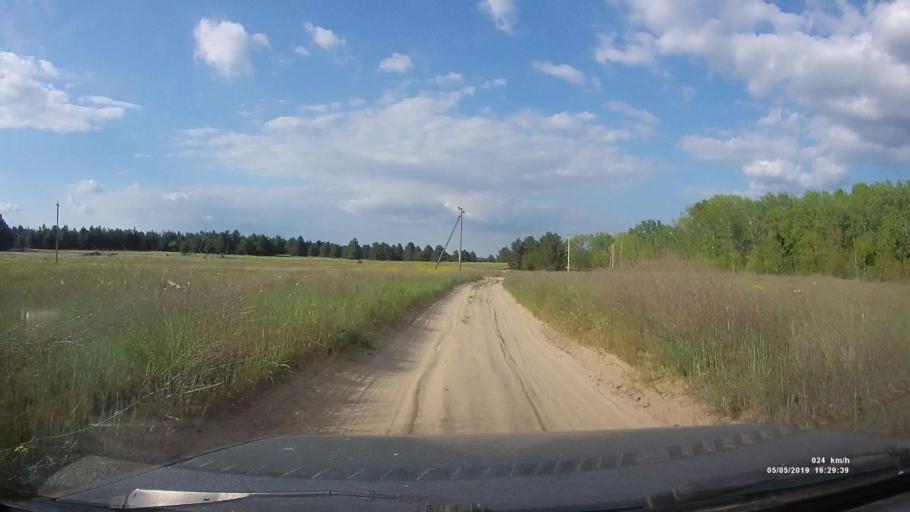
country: RU
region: Rostov
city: Ust'-Donetskiy
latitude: 47.7711
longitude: 41.0144
